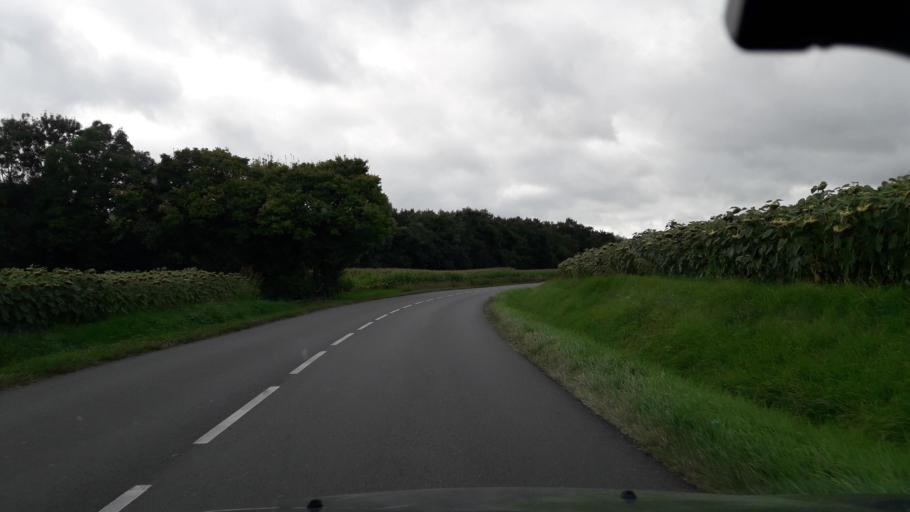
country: FR
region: Poitou-Charentes
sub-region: Departement de la Charente-Maritime
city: Saint-Sulpice-de-Royan
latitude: 45.6776
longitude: -0.9868
